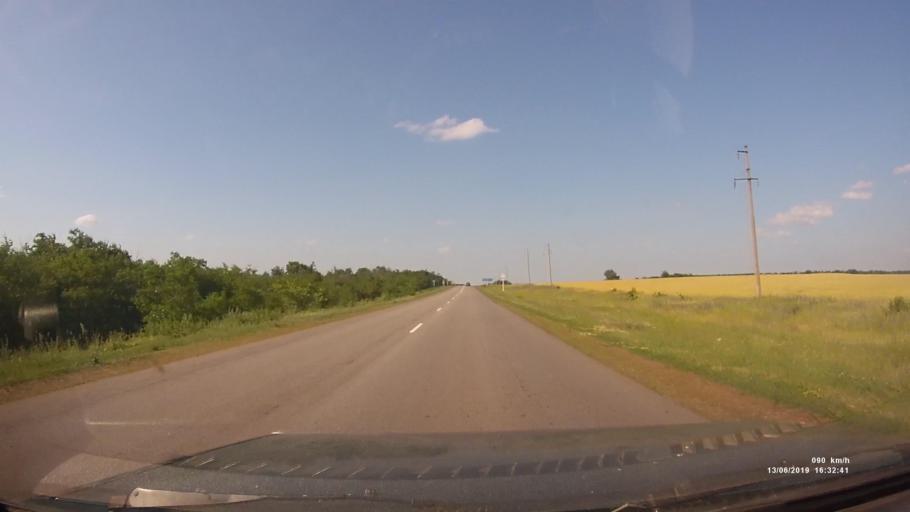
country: RU
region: Rostov
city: Kazanskaya
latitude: 49.8512
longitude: 41.2733
